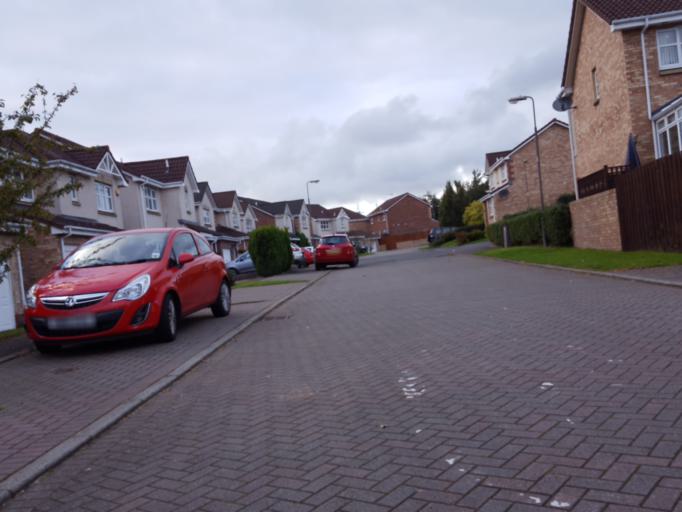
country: GB
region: Scotland
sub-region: West Lothian
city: Livingston
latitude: 55.8898
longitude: -3.5435
